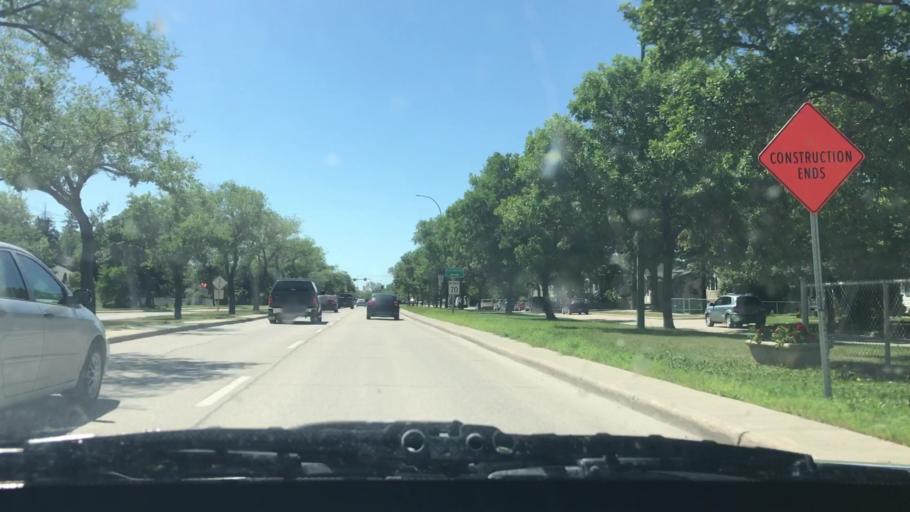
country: CA
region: Manitoba
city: Winnipeg
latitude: 49.8540
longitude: -97.1079
